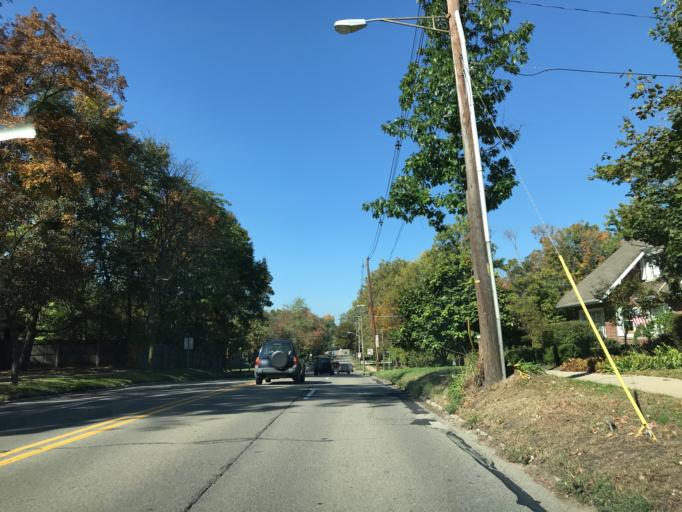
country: US
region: Michigan
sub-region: Washtenaw County
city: Ann Arbor
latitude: 42.2694
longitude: -83.7242
